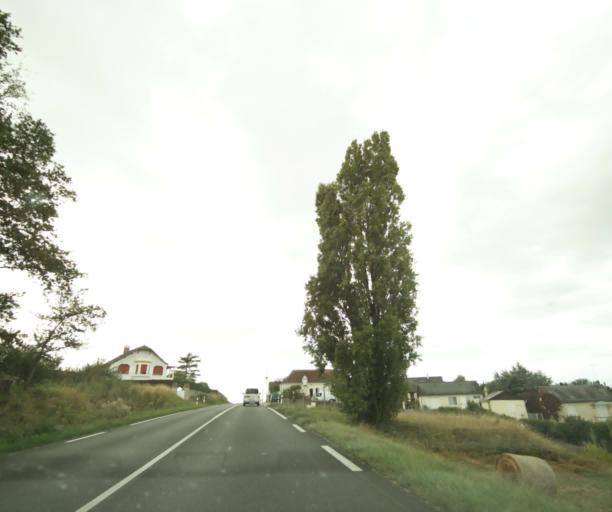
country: FR
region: Centre
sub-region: Departement d'Indre-et-Loire
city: Chambourg-sur-Indre
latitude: 47.1796
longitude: 0.9652
